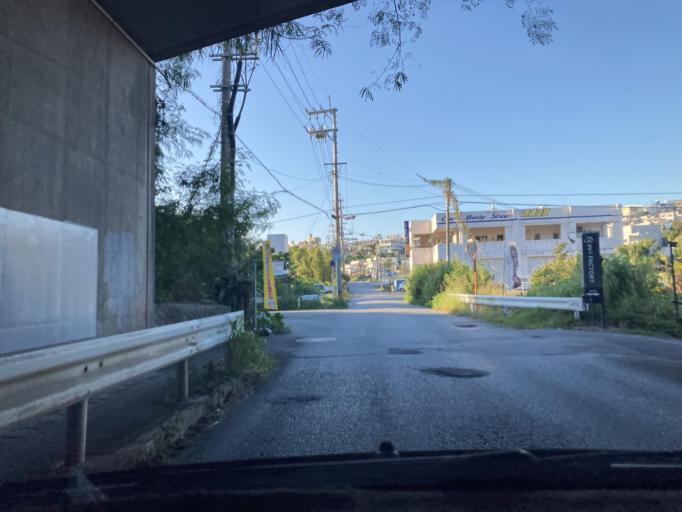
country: JP
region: Okinawa
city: Naha-shi
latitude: 26.2125
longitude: 127.7292
